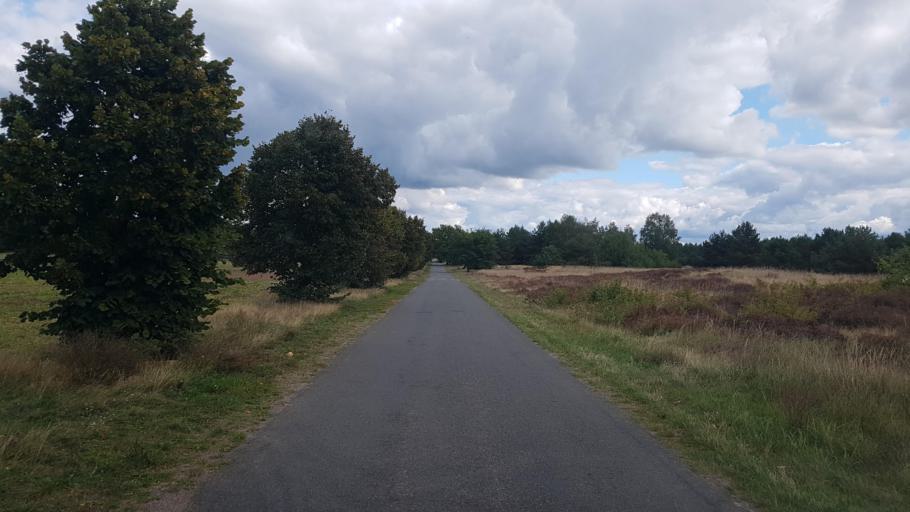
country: DE
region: Brandenburg
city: Linthe
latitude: 52.0696
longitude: 12.7896
